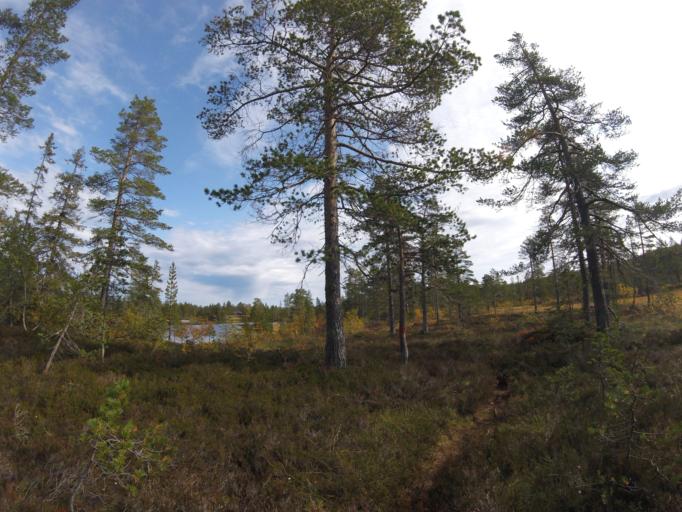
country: NO
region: Buskerud
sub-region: Rollag
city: Rollag
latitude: 59.8166
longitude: 9.3486
